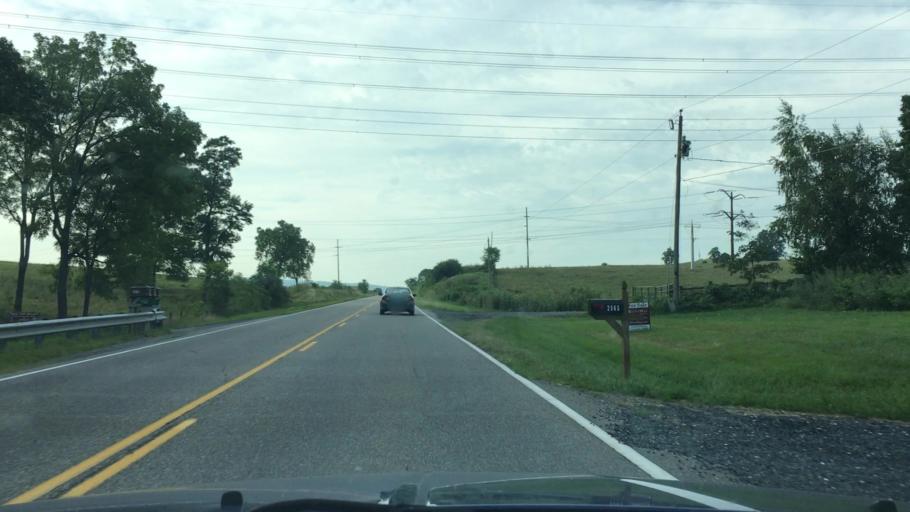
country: US
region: Virginia
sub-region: Augusta County
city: Dooms
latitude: 38.1226
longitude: -78.9135
